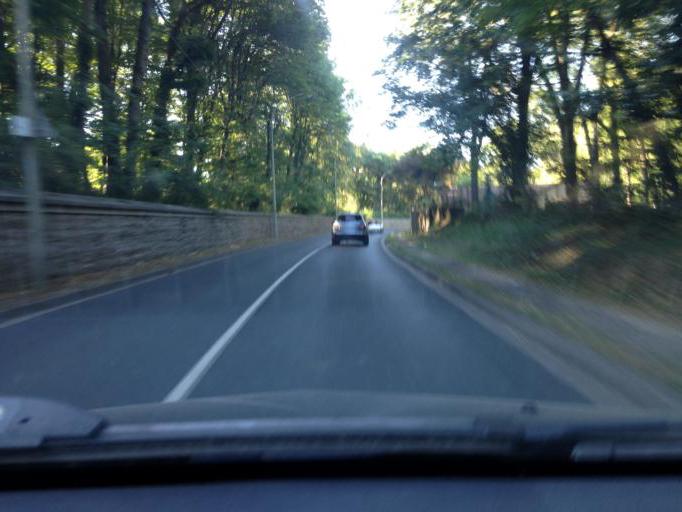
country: FR
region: Ile-de-France
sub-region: Departement des Yvelines
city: Saint-Remy-les-Chevreuse
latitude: 48.7111
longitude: 2.0846
